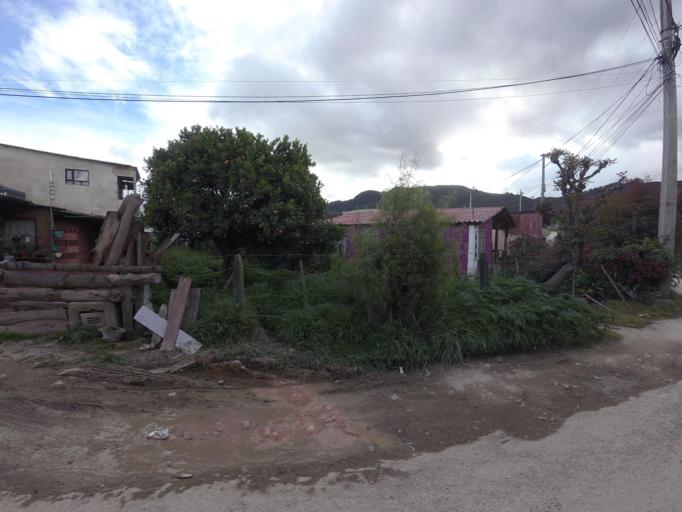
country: CO
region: Cundinamarca
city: Tabio
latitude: 4.9273
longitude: -74.0924
